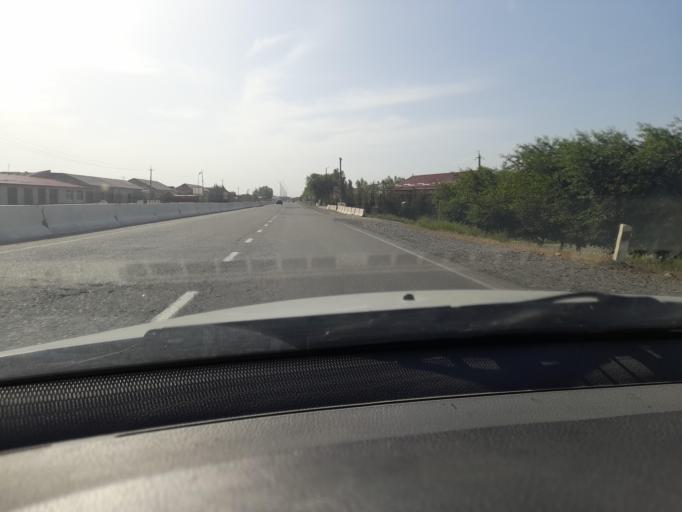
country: UZ
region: Samarqand
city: Kattaqo'rg'on
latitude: 39.9207
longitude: 66.2930
